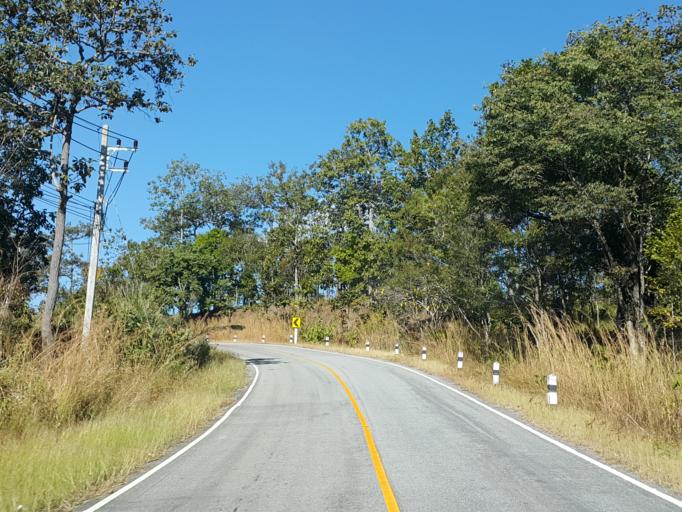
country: TH
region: Chiang Mai
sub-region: Amphoe Chiang Dao
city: Chiang Dao
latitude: 19.5276
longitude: 98.8916
